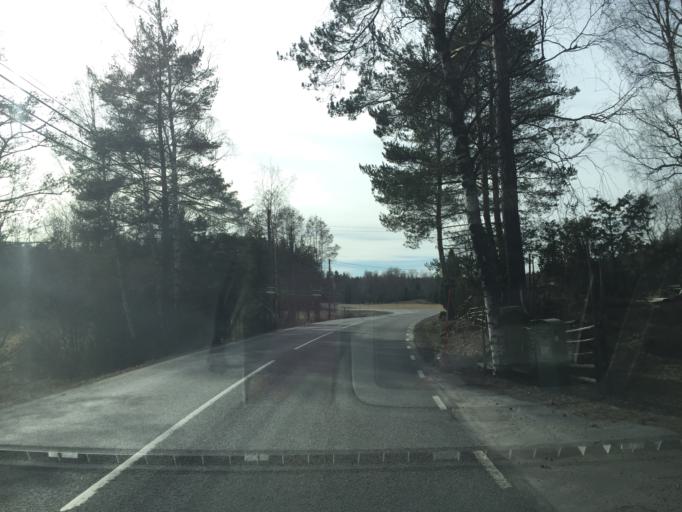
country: SE
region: Stockholm
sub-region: Haninge Kommun
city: Jordbro
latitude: 59.1154
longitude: 18.0141
